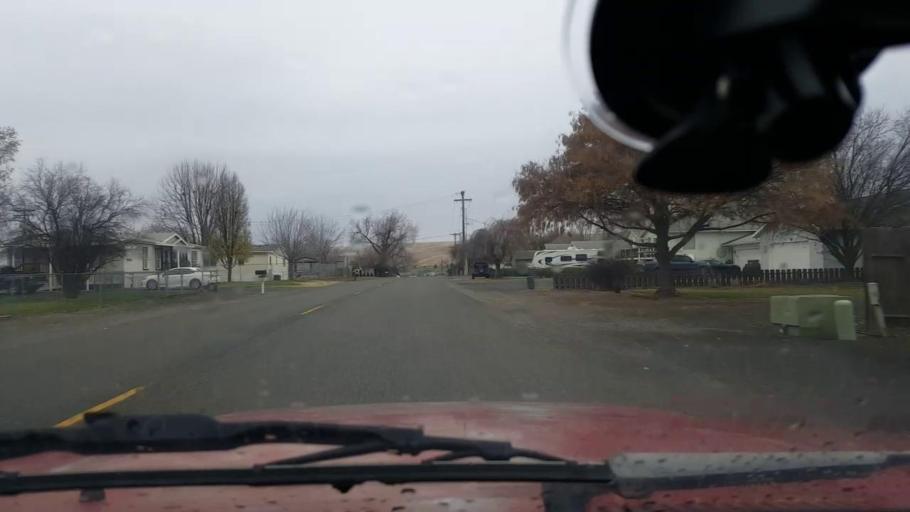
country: US
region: Washington
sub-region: Asotin County
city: Clarkston Heights-Vineland
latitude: 46.3826
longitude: -117.0856
